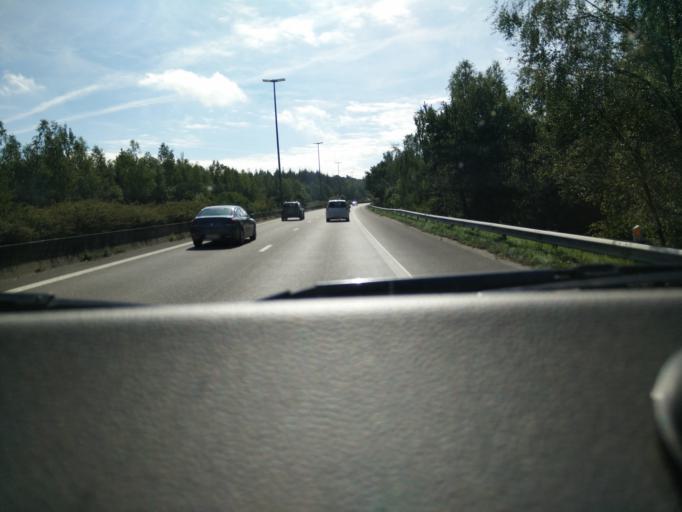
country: BE
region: Wallonia
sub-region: Province du Luxembourg
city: Tellin
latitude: 50.0602
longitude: 5.2016
